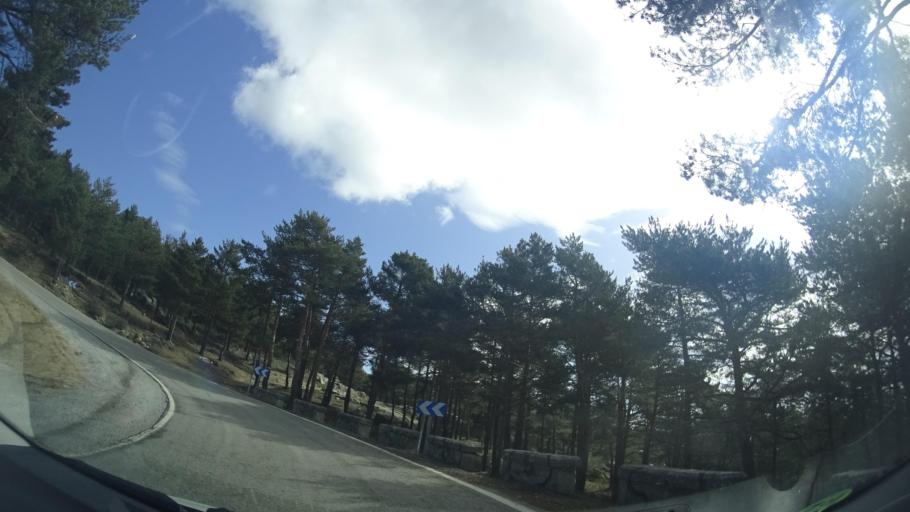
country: ES
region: Madrid
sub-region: Provincia de Madrid
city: Canencia
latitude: 40.8660
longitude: -3.7598
